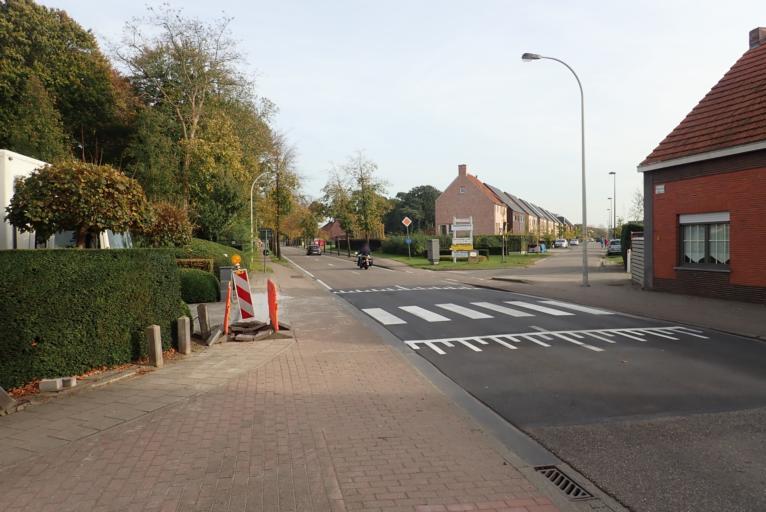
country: BE
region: Flanders
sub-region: Provincie Antwerpen
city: Wuustwezel
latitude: 51.3913
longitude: 4.5702
